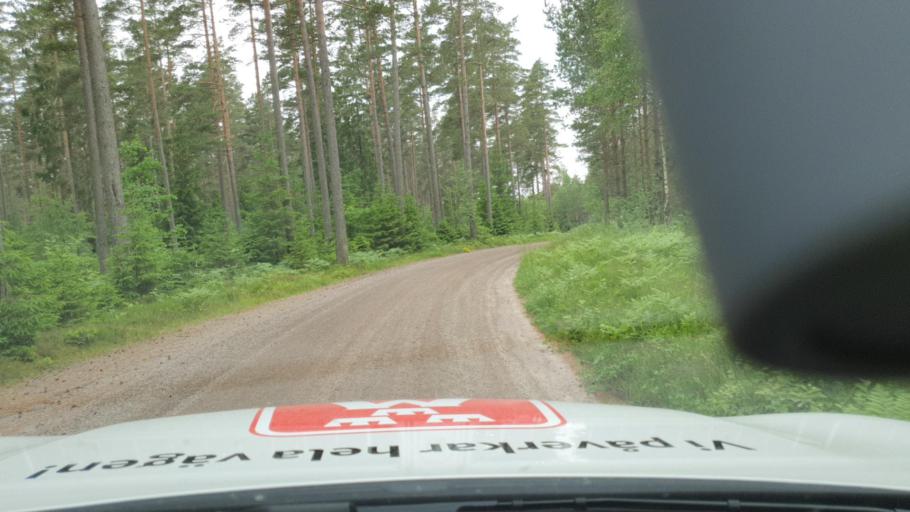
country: SE
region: Vaestra Goetaland
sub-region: Hjo Kommun
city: Hjo
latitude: 58.3398
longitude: 14.2817
